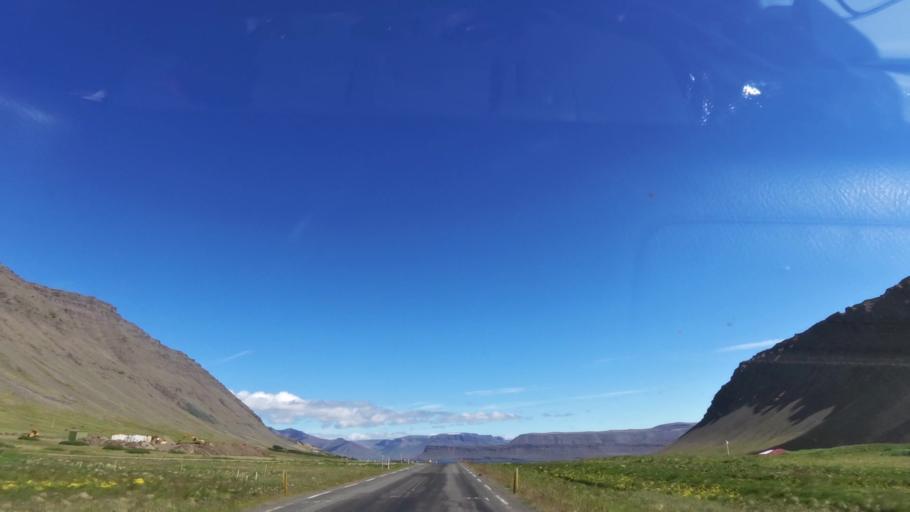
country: IS
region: Westfjords
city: Isafjoerdur
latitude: 65.6709
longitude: -23.6251
